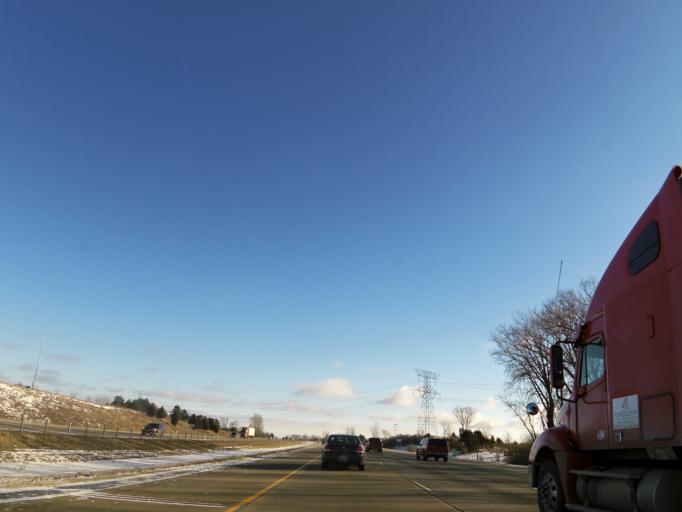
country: US
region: Minnesota
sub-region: Washington County
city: Lakeland
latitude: 44.9486
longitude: -92.8221
